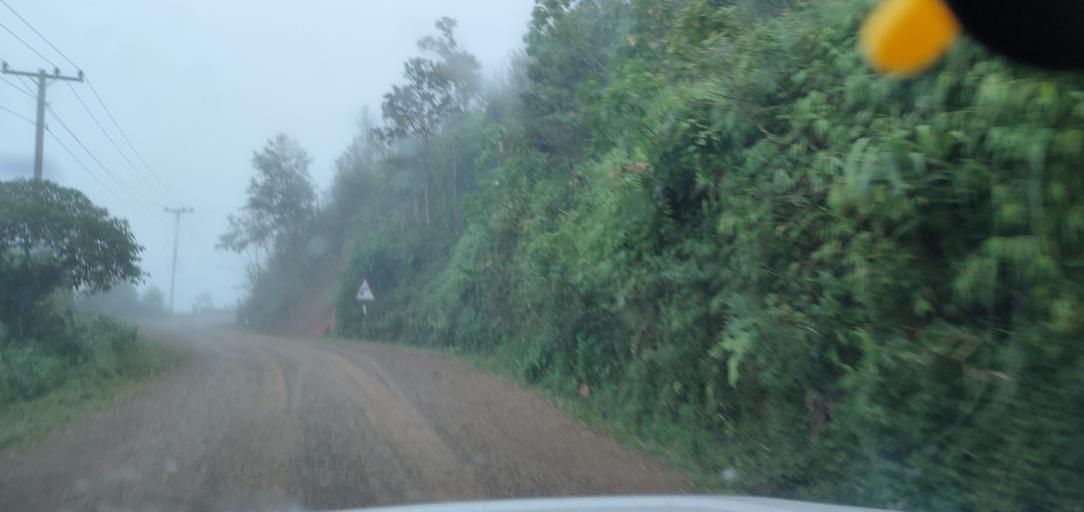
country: LA
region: Phongsali
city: Phongsali
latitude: 21.3983
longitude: 102.1916
